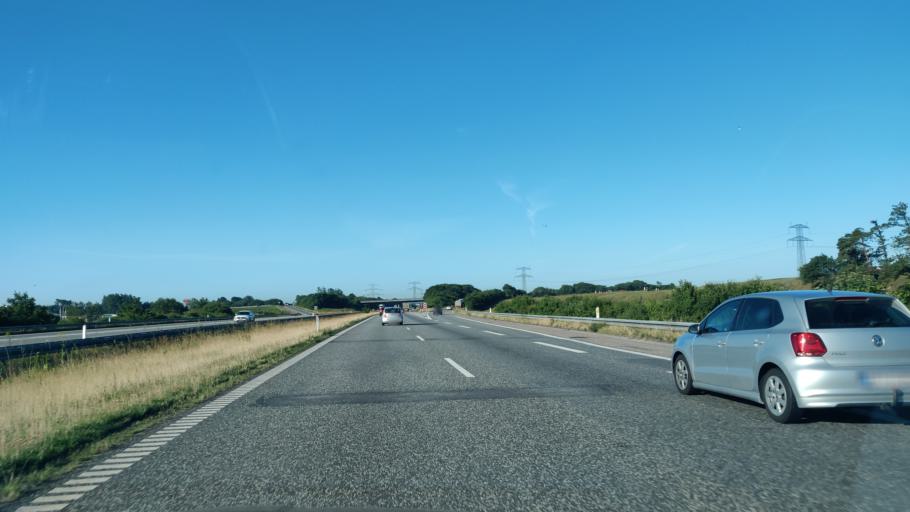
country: DK
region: North Denmark
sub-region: Rebild Kommune
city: Stovring
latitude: 56.8836
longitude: 9.8065
